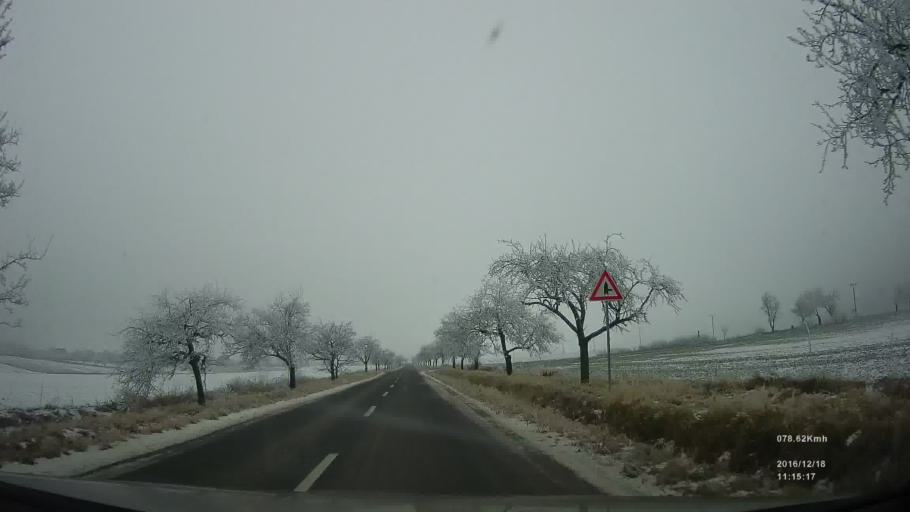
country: SK
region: Presovsky
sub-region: Okres Presov
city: Presov
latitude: 48.9032
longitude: 21.3233
